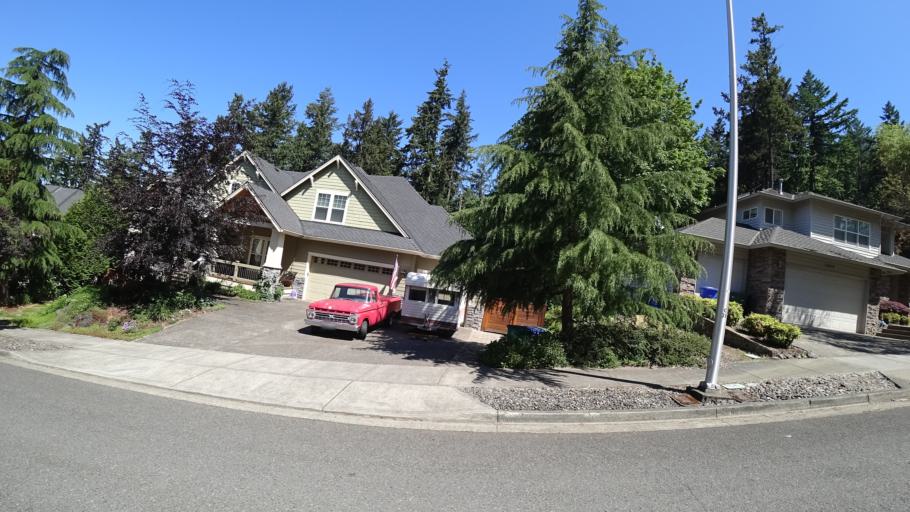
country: US
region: Oregon
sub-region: Clackamas County
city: Happy Valley
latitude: 45.4635
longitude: -122.5231
